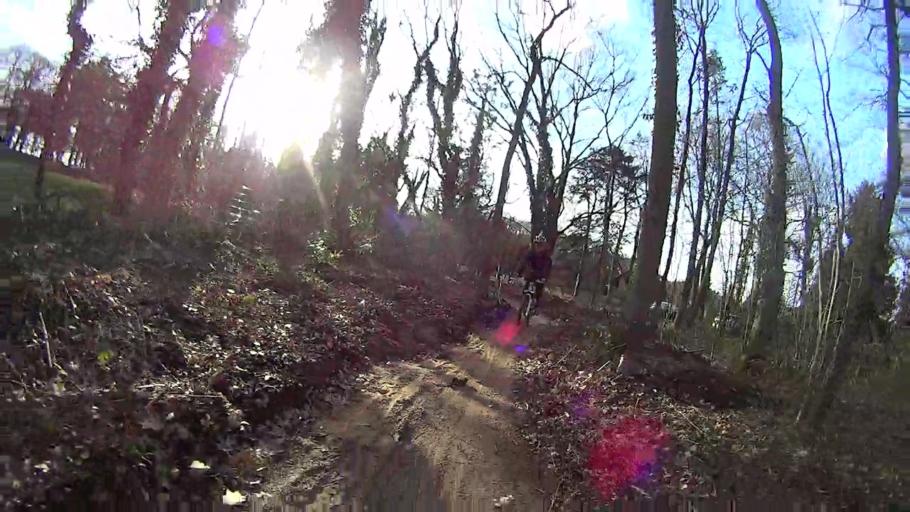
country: NL
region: Utrecht
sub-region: Gemeente Utrechtse Heuvelrug
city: Driebergen-Rijsenburg
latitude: 52.0657
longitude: 5.2736
